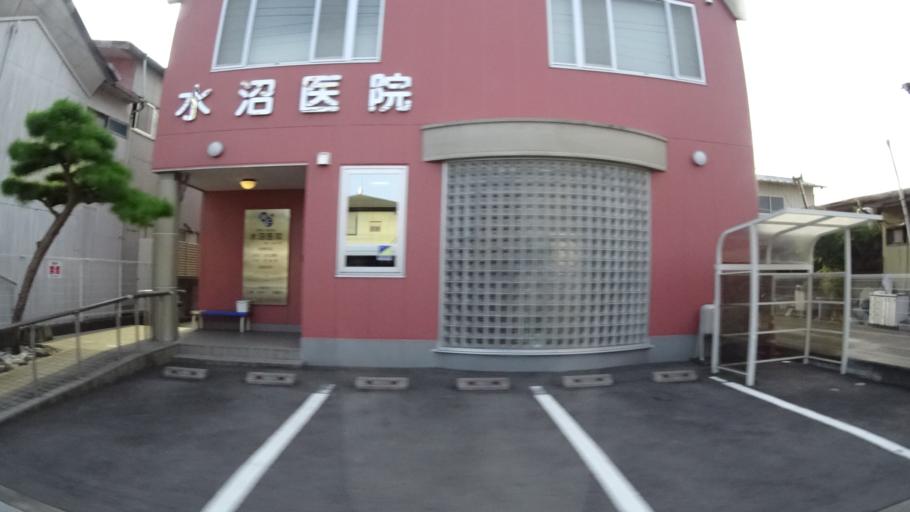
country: JP
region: Tochigi
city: Karasuyama
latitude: 36.6513
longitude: 140.1527
